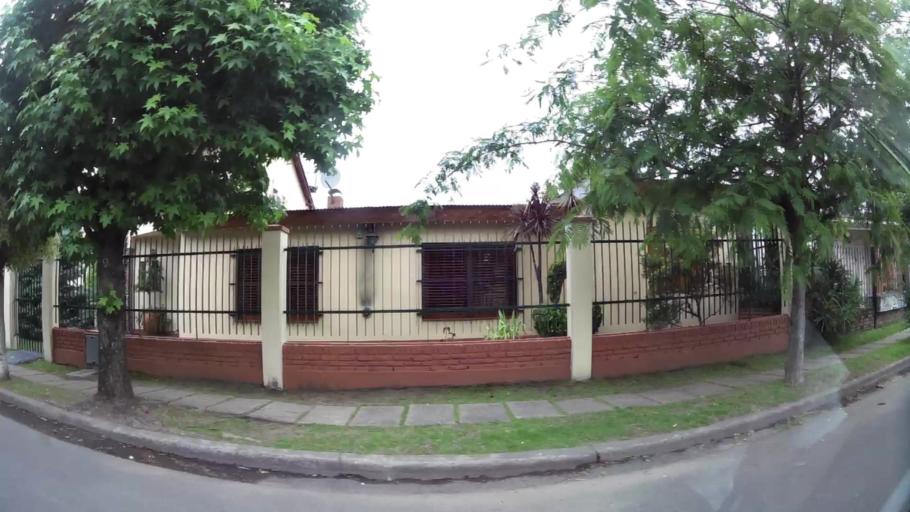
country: AR
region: Buenos Aires
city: San Justo
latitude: -34.7353
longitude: -58.5281
